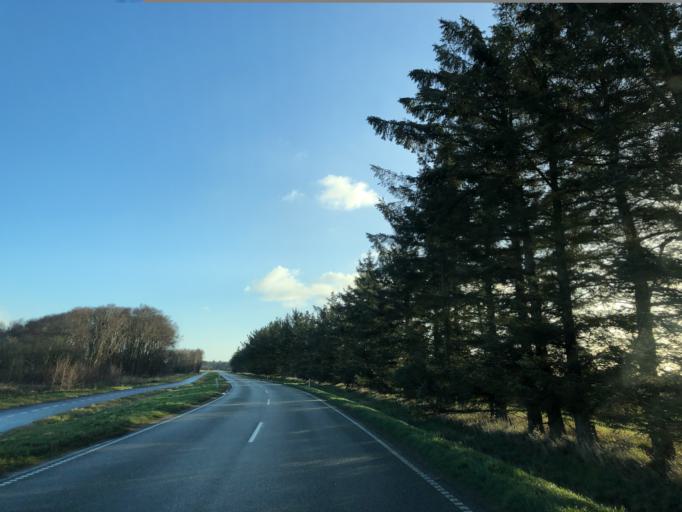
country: DK
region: Central Jutland
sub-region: Holstebro Kommune
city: Ulfborg
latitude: 56.2007
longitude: 8.2670
